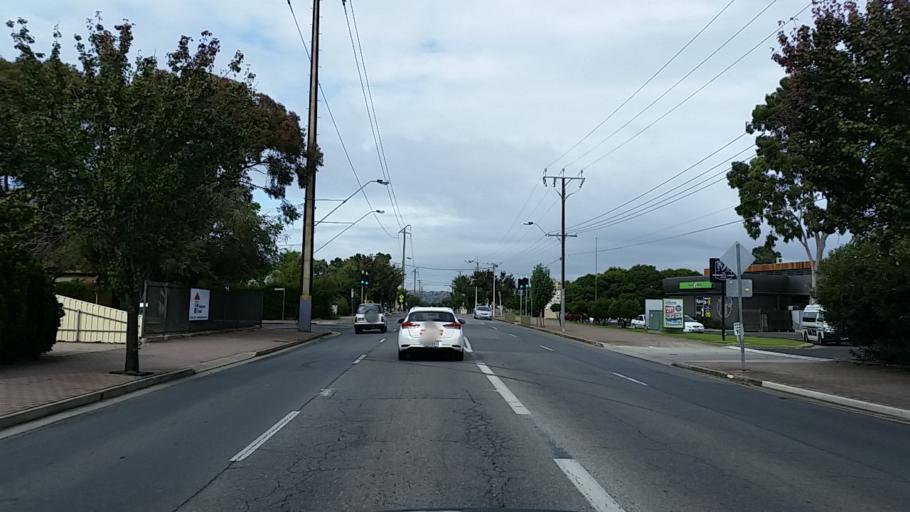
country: AU
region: South Australia
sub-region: Marion
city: Plympton Park
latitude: -34.9863
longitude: 138.5385
